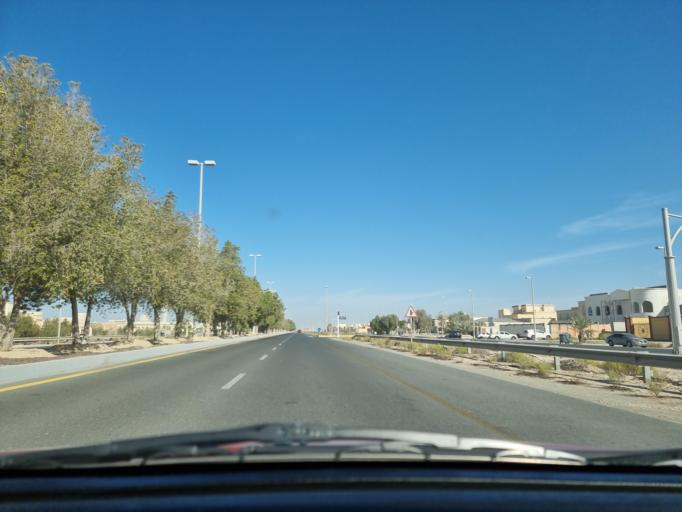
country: AE
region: Abu Dhabi
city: Abu Dhabi
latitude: 24.3880
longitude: 54.6952
